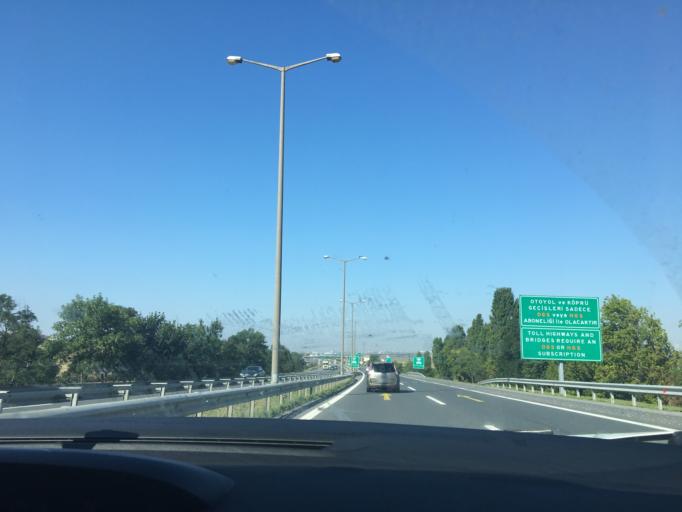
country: TR
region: Istanbul
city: Silivri
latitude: 41.1143
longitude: 28.1727
